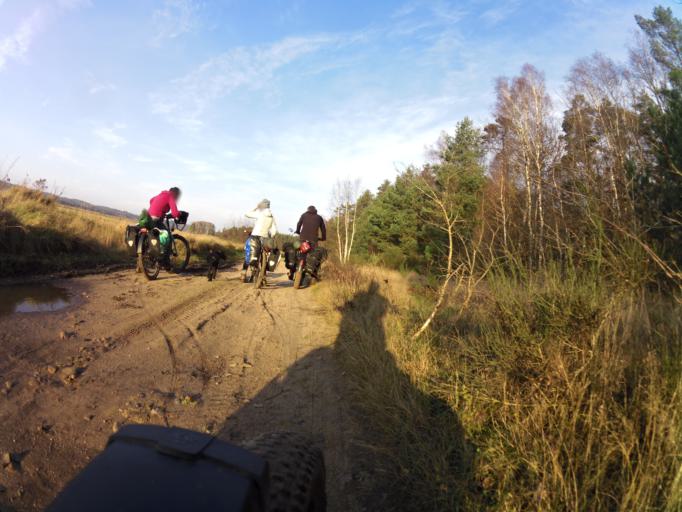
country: PL
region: West Pomeranian Voivodeship
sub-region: Powiat koszalinski
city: Polanow
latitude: 54.1033
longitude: 16.6488
